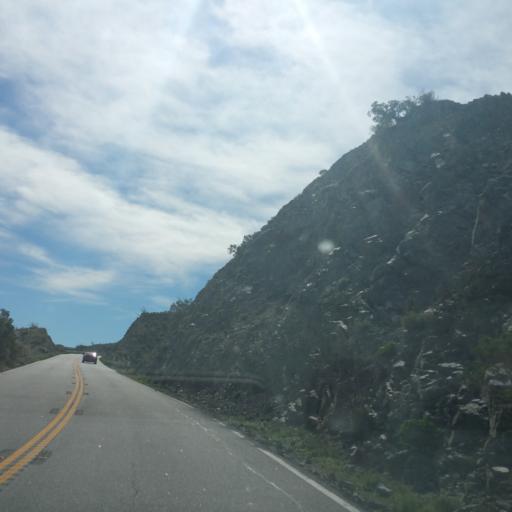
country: US
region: California
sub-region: Riverside County
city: Palm Desert
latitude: 33.6539
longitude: -116.4013
